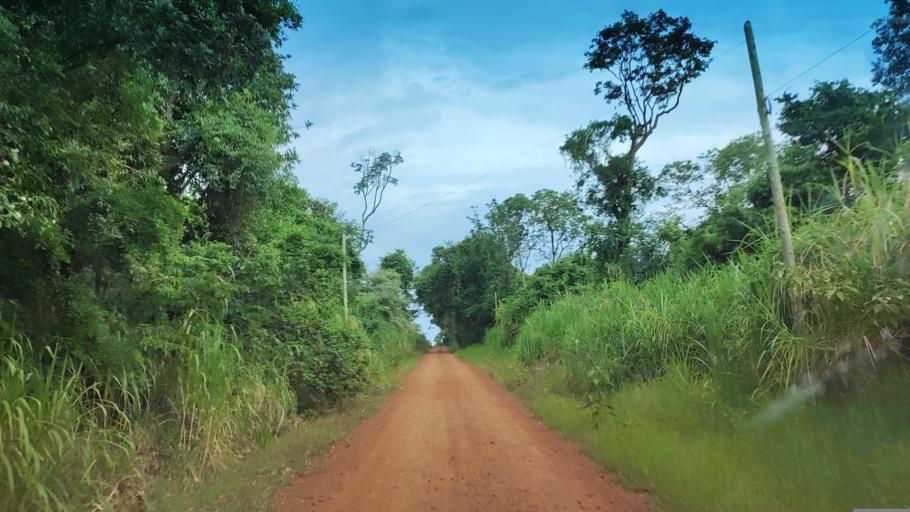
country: AR
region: Misiones
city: Gobernador Roca
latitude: -27.1467
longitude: -55.4765
